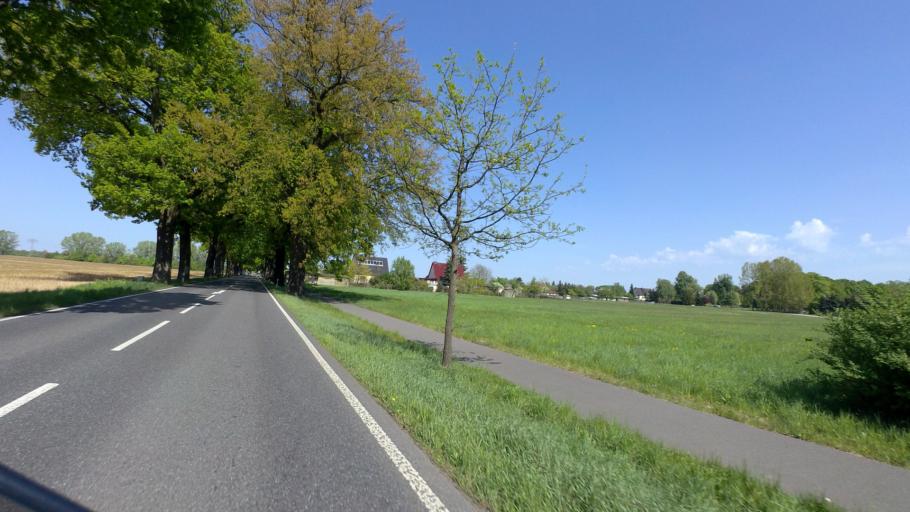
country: DE
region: Brandenburg
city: Beeskow
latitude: 52.1824
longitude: 14.2819
